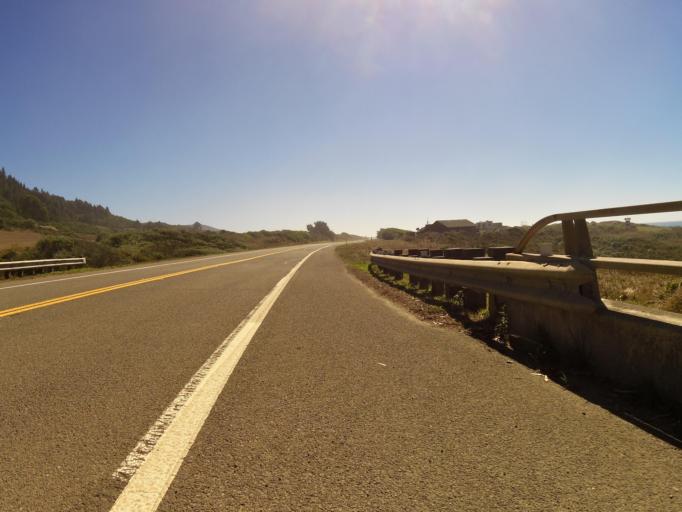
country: US
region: California
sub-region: Mendocino County
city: Fort Bragg
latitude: 39.6773
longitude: -123.7900
